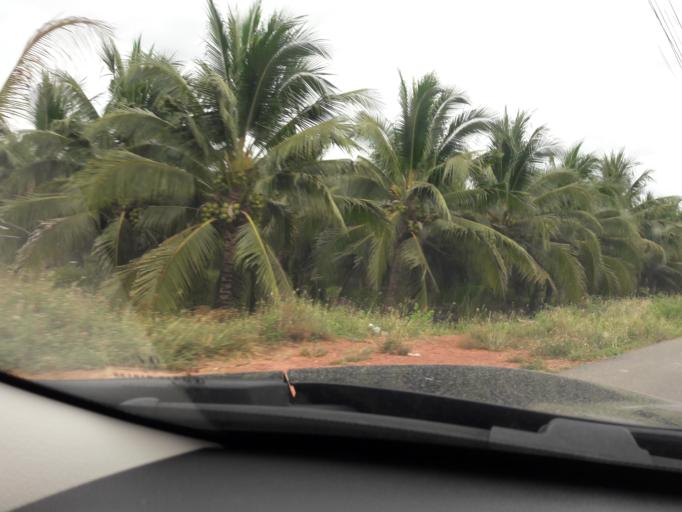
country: TH
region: Ratchaburi
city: Bang Phae
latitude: 13.6277
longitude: 99.9522
